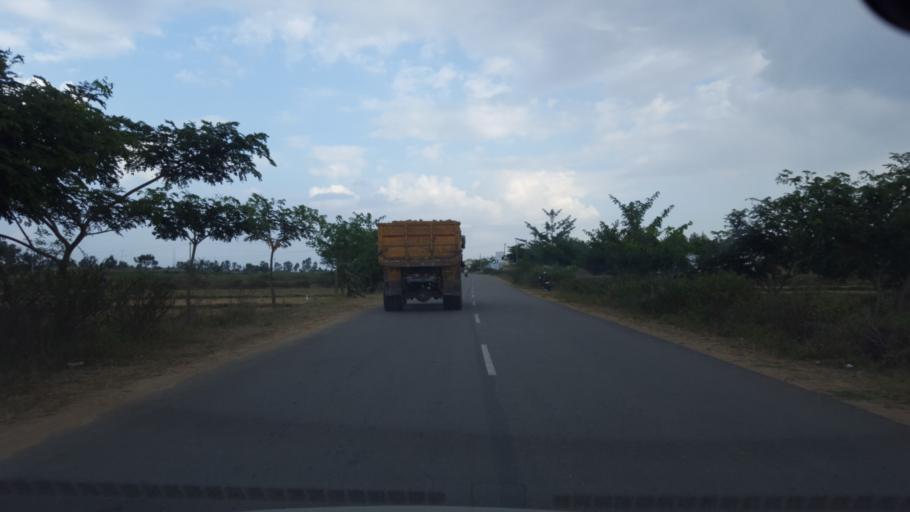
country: IN
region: Telangana
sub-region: Mahbubnagar
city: Mahbubnagar
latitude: 16.7609
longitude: 77.9544
